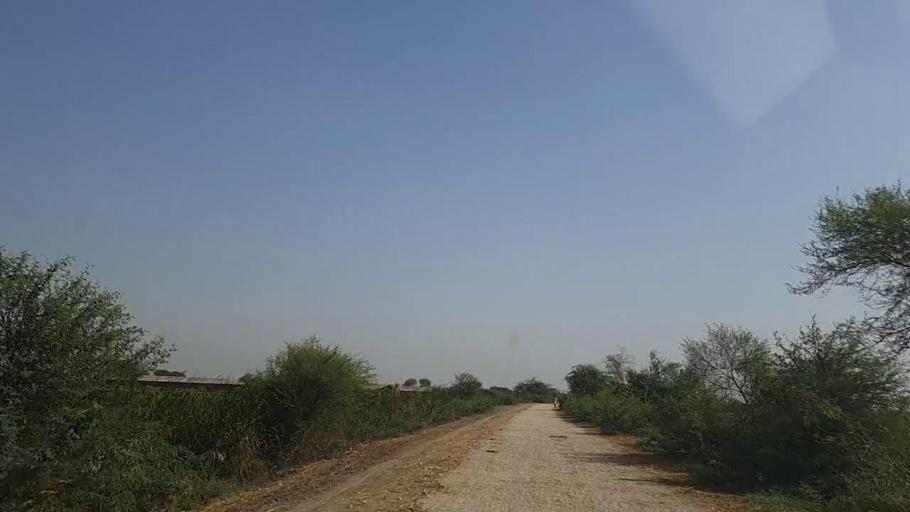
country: PK
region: Sindh
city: Daro Mehar
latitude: 24.7196
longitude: 68.0831
